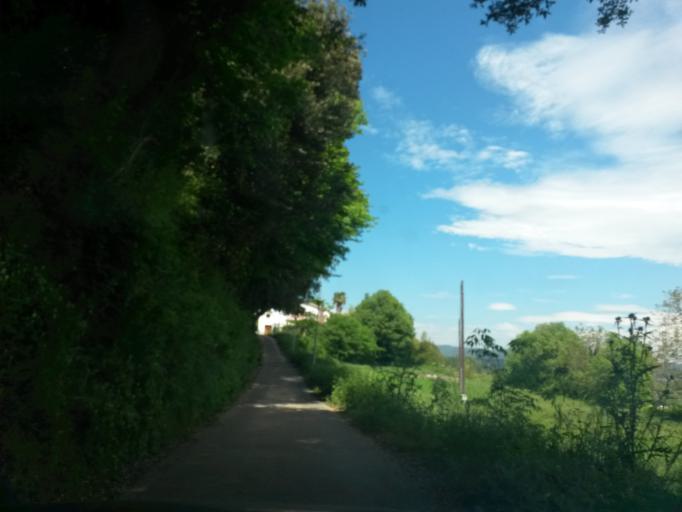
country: ES
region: Catalonia
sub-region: Provincia de Girona
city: Vilablareix
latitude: 41.9677
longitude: 2.7606
